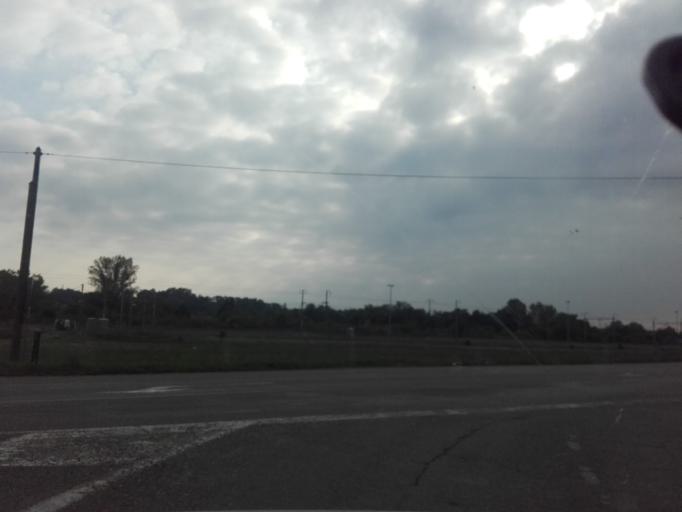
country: FR
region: Bourgogne
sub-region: Departement de Saone-et-Loire
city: Charnay-les-Macon
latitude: 46.2975
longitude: 4.7667
